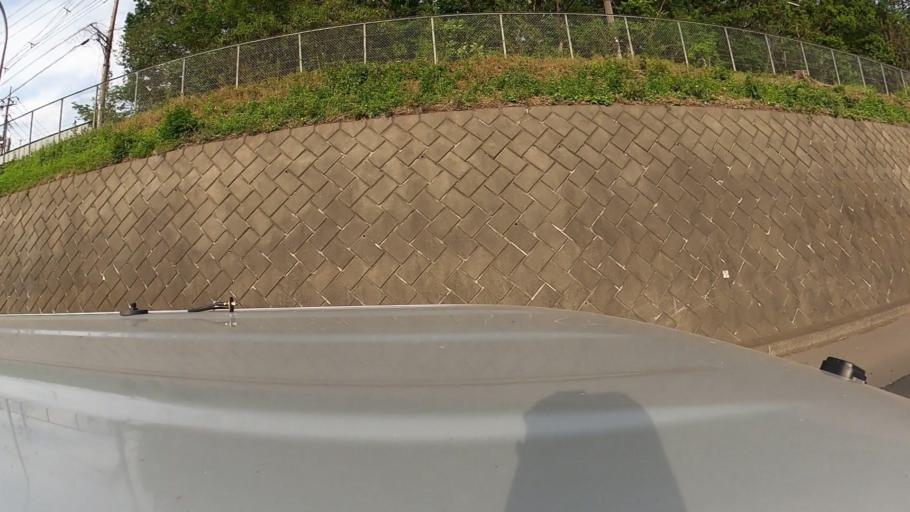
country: JP
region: Saitama
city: Oi
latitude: 35.8389
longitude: 139.5041
